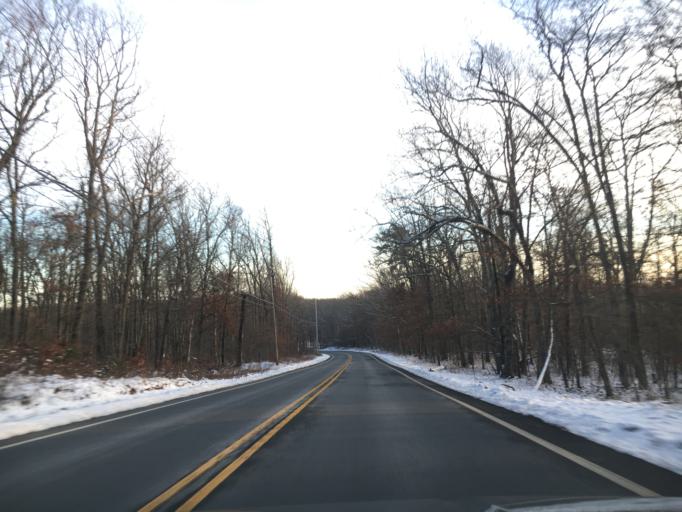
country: US
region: Pennsylvania
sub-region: Pike County
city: Hemlock Farms
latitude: 41.2669
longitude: -75.0839
